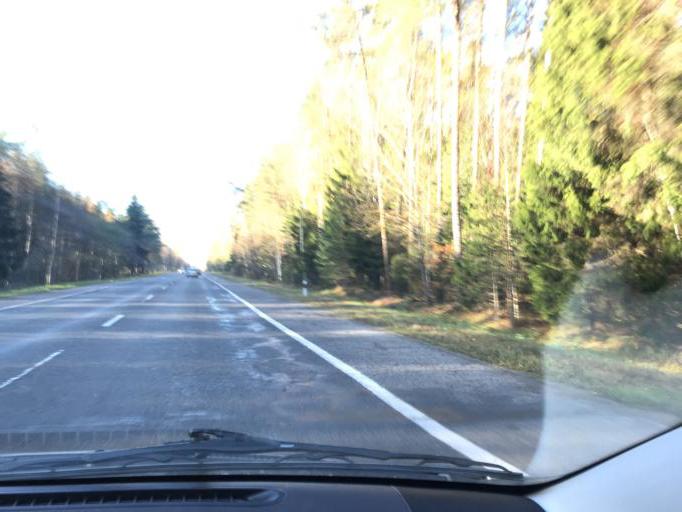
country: BY
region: Vitebsk
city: Syanno
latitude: 55.0720
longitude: 29.5520
